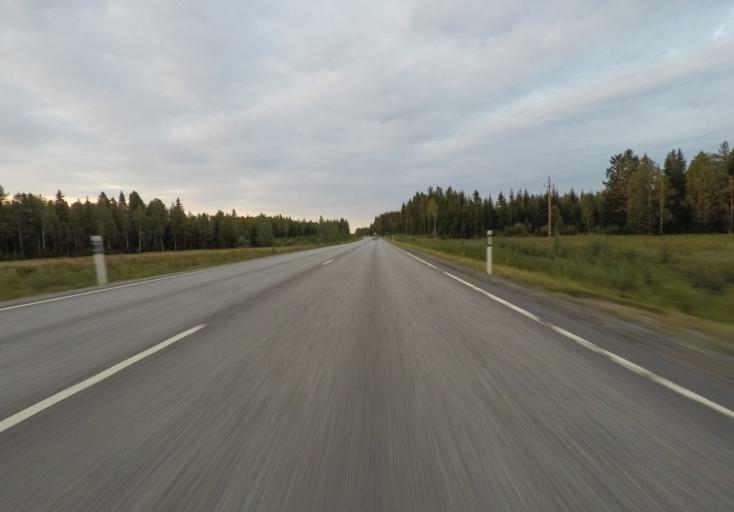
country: FI
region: Central Finland
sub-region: Jyvaeskylae
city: Hankasalmi
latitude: 62.3799
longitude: 26.5948
